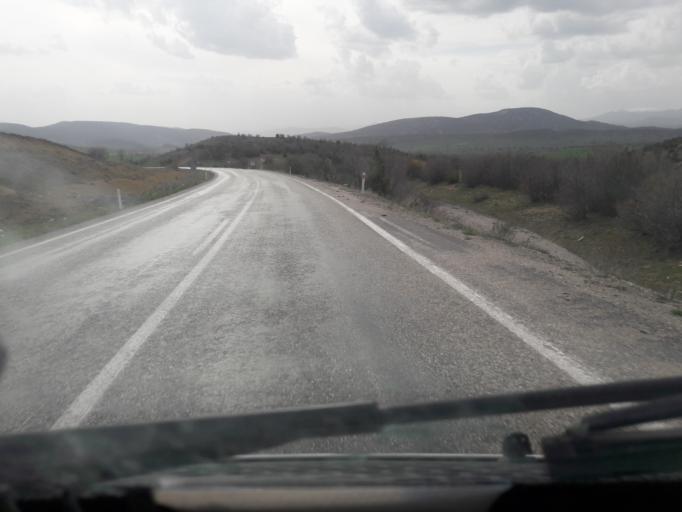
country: TR
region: Gumushane
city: Evren
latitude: 40.1720
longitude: 39.2387
